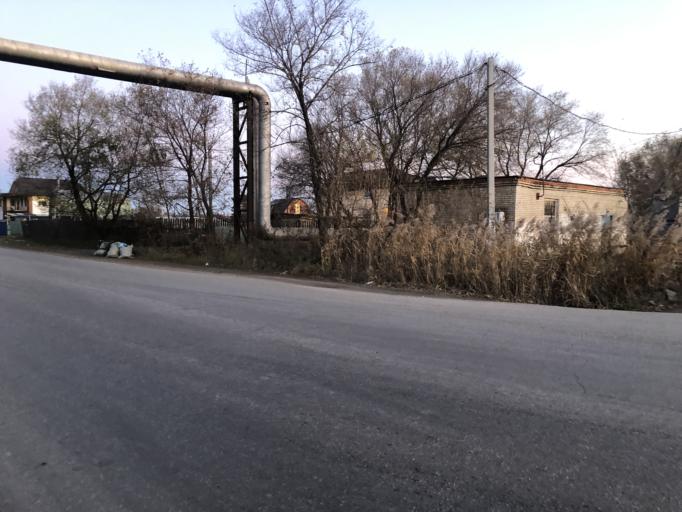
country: RU
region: Khabarovsk Krai
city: Topolevo
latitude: 48.4551
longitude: 135.1984
